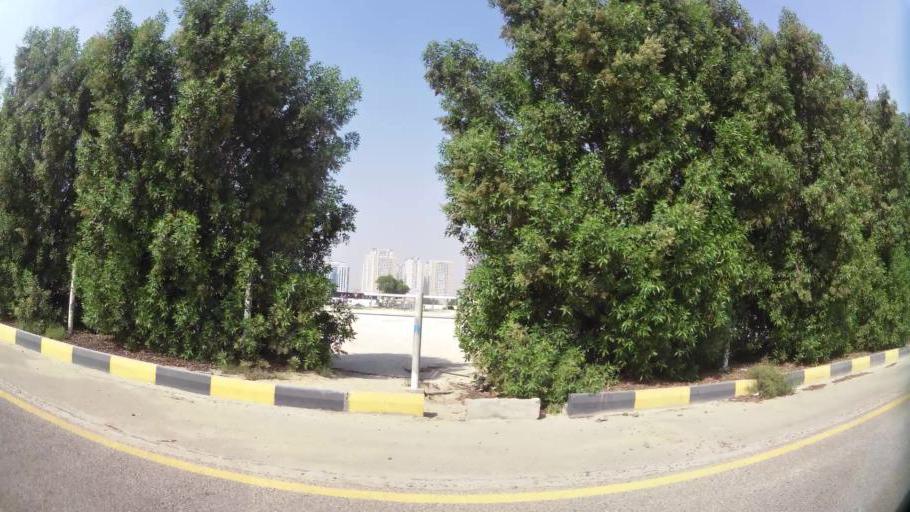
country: AE
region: Ajman
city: Ajman
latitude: 25.3890
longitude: 55.4215
